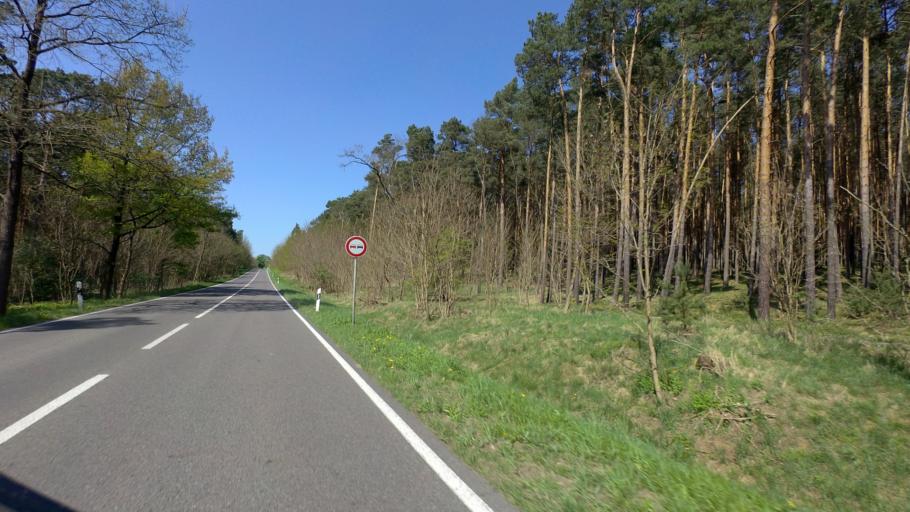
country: DE
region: Brandenburg
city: Lieberose
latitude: 52.0332
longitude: 14.2986
